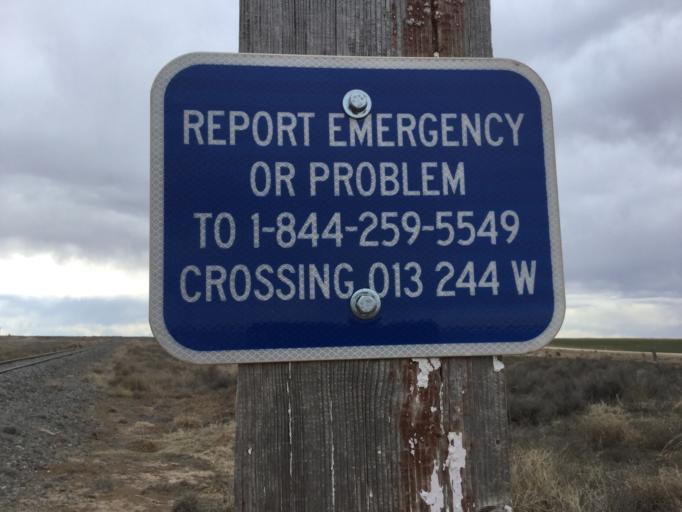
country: US
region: Kansas
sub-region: Morton County
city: Elkhart
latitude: 37.0685
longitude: -101.7909
